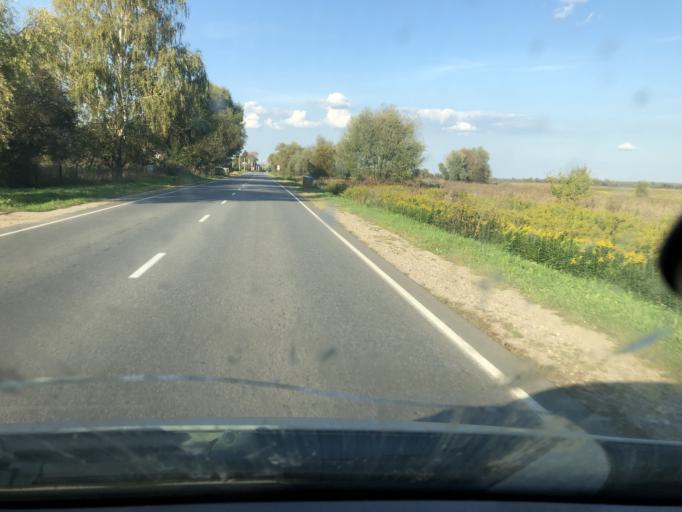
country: RU
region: Kaluga
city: Sosenskiy
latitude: 54.1379
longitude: 35.8851
